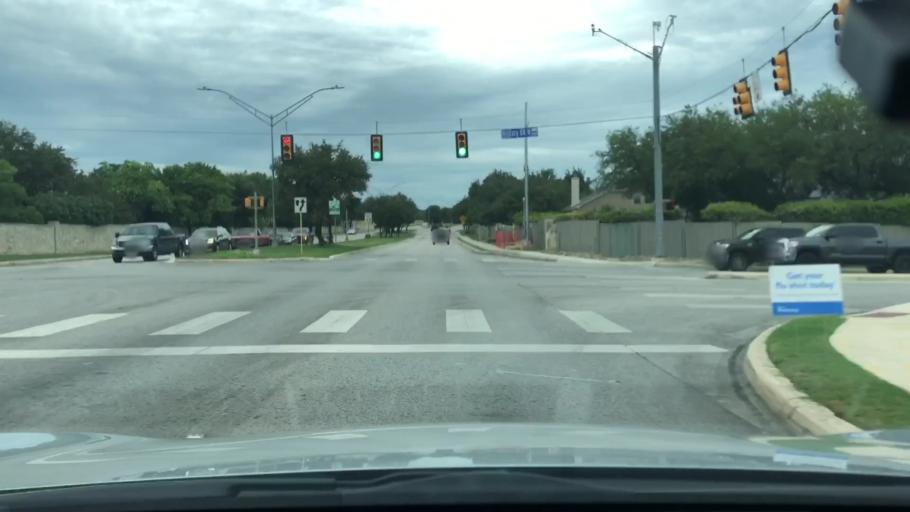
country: US
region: Texas
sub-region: Bexar County
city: Leon Valley
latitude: 29.4596
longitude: -98.6716
